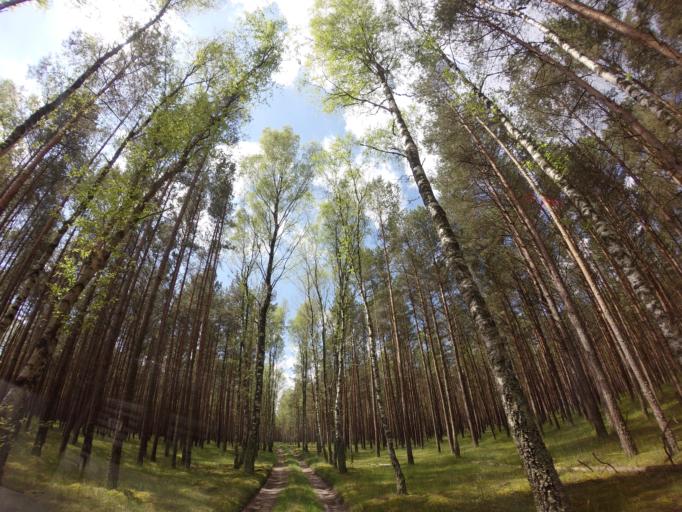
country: PL
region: West Pomeranian Voivodeship
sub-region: Powiat drawski
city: Kalisz Pomorski
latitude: 53.2112
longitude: 15.9471
